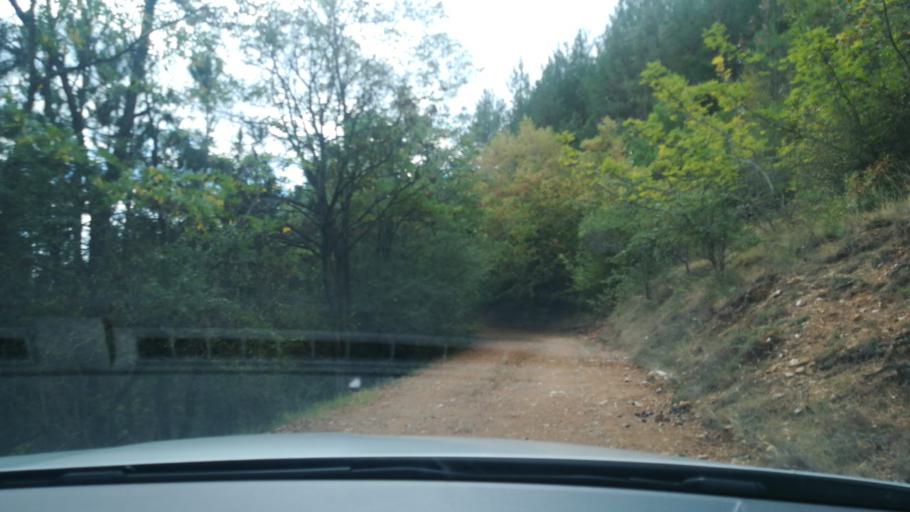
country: MK
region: Makedonska Kamenica
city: Makedonska Kamenica
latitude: 42.0048
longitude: 22.6059
